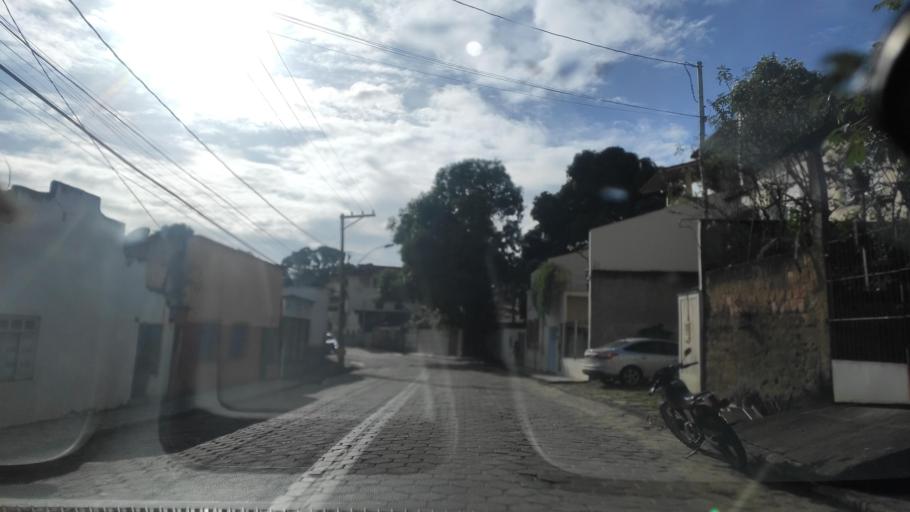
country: BR
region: Espirito Santo
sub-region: Nova Venecia
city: Nova Venecia
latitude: -18.7133
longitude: -40.3929
